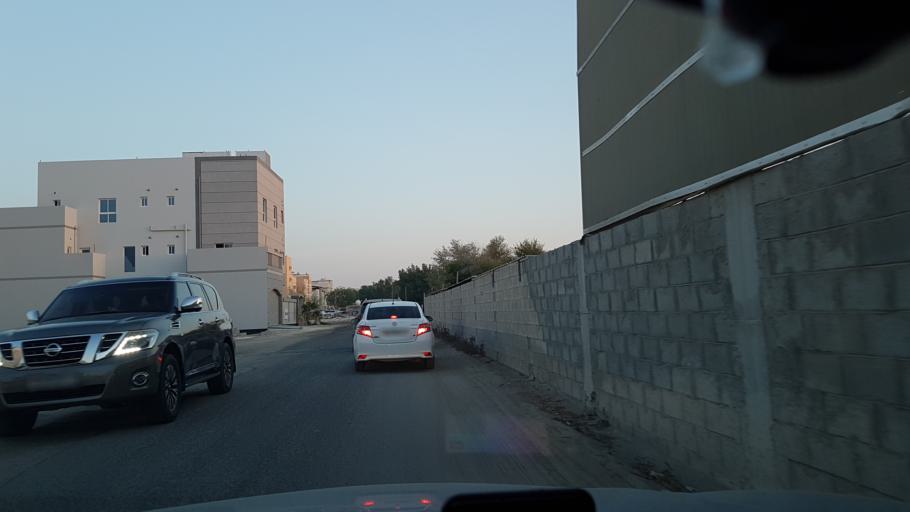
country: BH
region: Manama
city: Jidd Hafs
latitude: 26.2325
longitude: 50.5058
